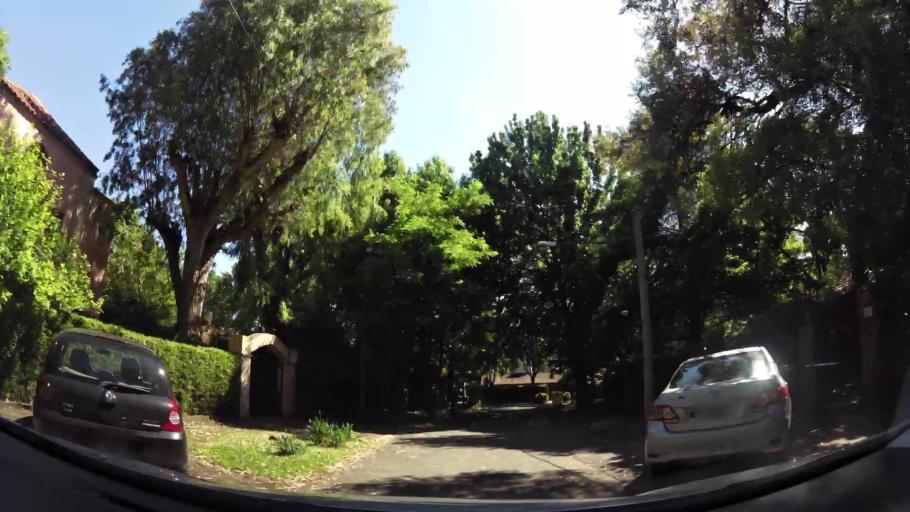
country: AR
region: Buenos Aires
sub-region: Partido de San Isidro
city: San Isidro
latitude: -34.4929
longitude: -58.5693
